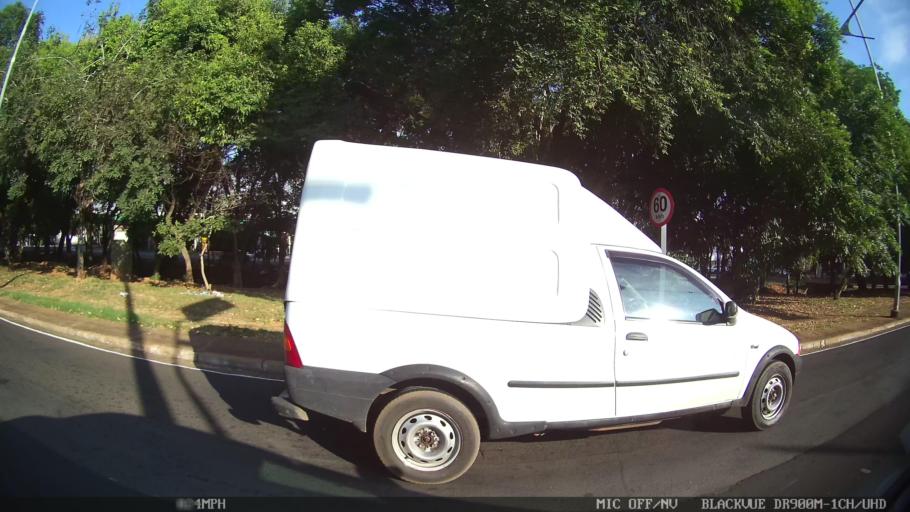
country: BR
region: Sao Paulo
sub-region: Sao Jose Do Rio Preto
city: Sao Jose do Rio Preto
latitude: -20.8198
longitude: -49.3656
